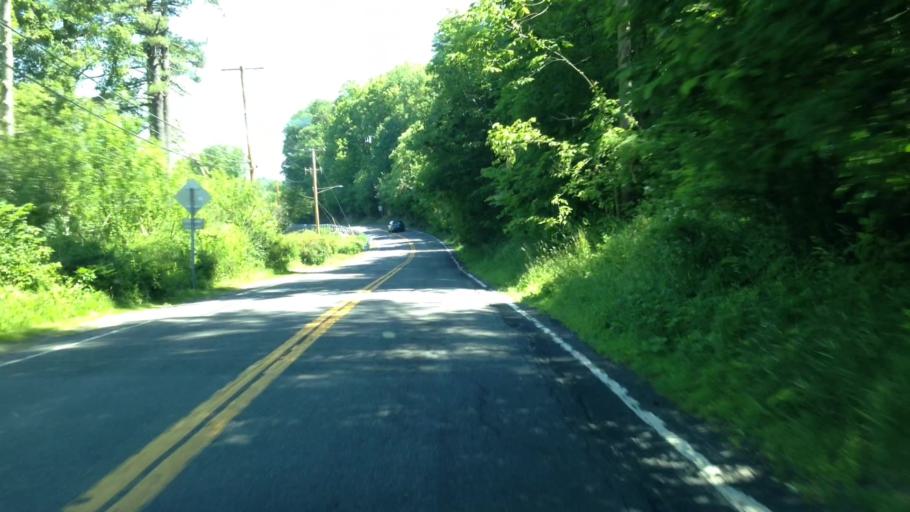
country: US
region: New York
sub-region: Ulster County
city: Tillson
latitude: 41.8329
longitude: -74.0454
